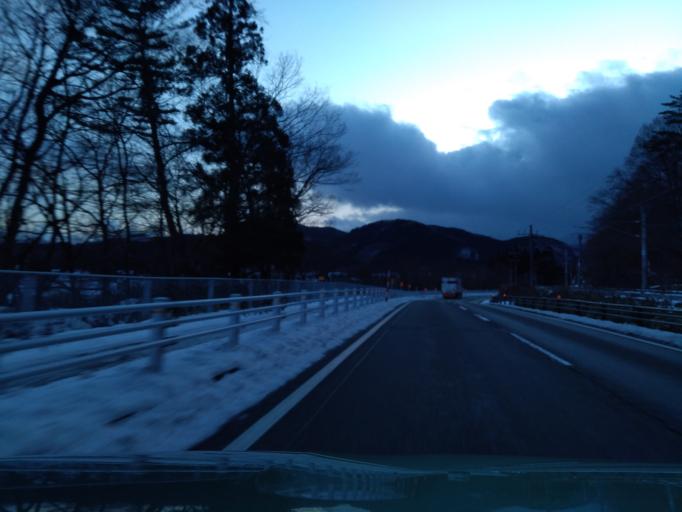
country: JP
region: Iwate
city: Shizukuishi
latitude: 39.6899
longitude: 140.9233
